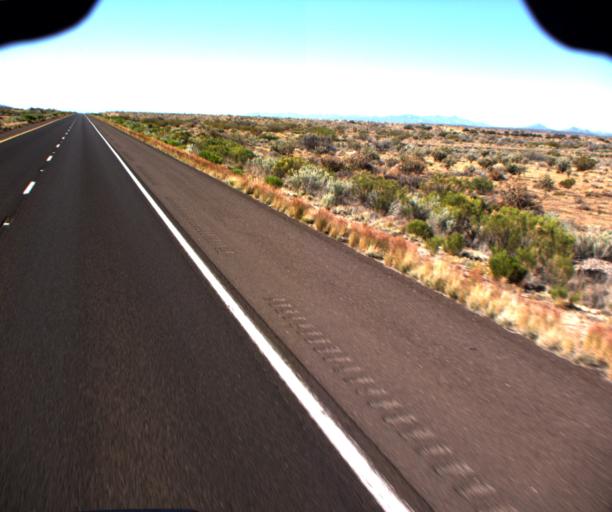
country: US
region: Arizona
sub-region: Mohave County
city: Kingman
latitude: 35.1211
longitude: -113.6669
